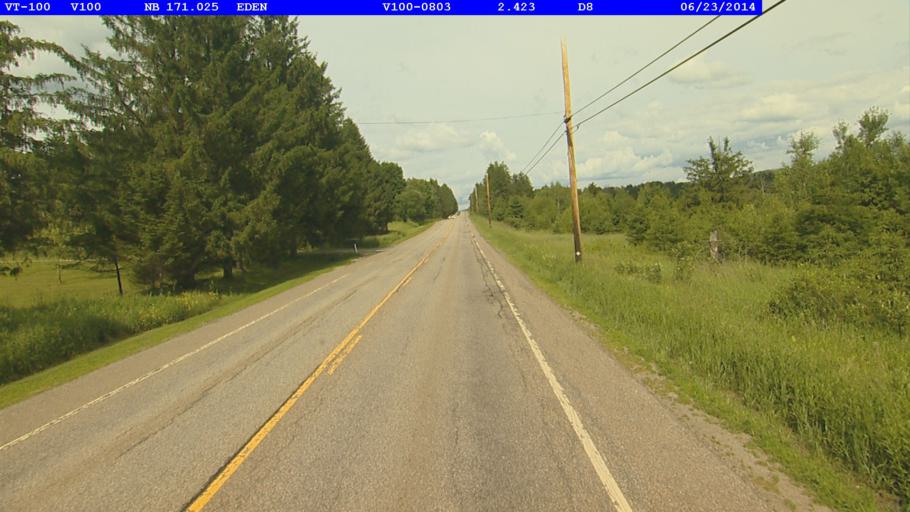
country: US
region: Vermont
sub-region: Lamoille County
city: Hyde Park
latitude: 44.7048
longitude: -72.5543
